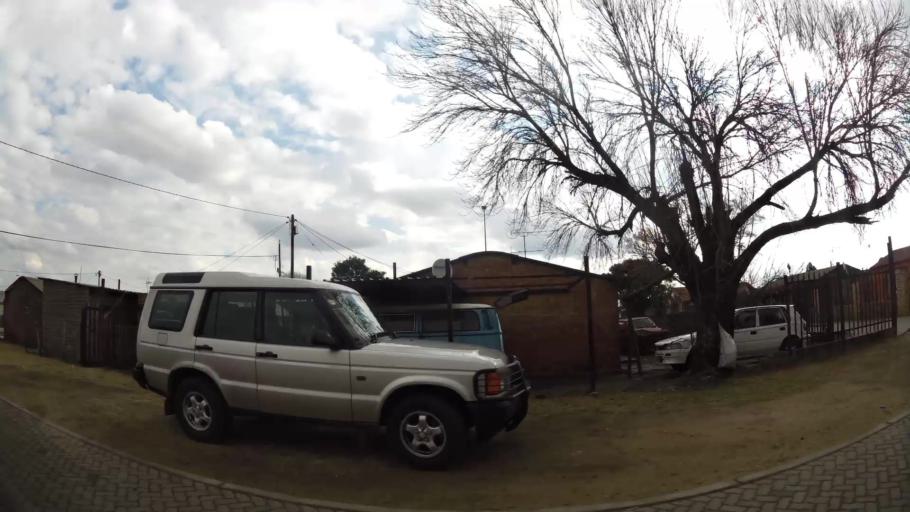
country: ZA
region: Orange Free State
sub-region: Fezile Dabi District Municipality
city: Sasolburg
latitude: -26.8406
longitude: 27.8504
